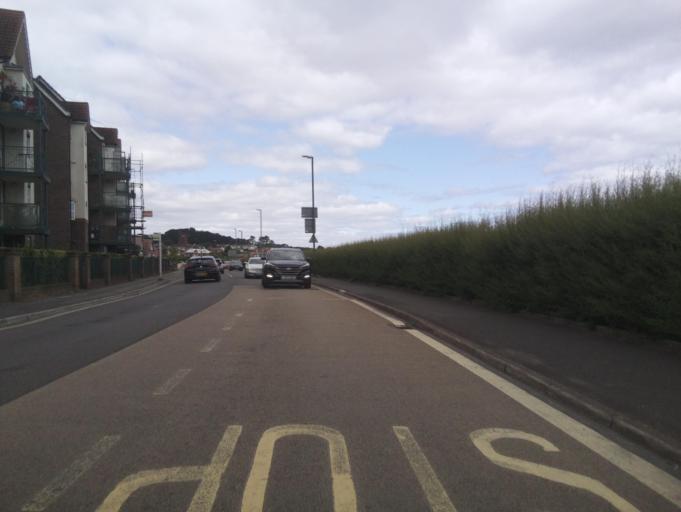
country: GB
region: England
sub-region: Borough of Torbay
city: Paignton
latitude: 50.4421
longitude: -3.5584
